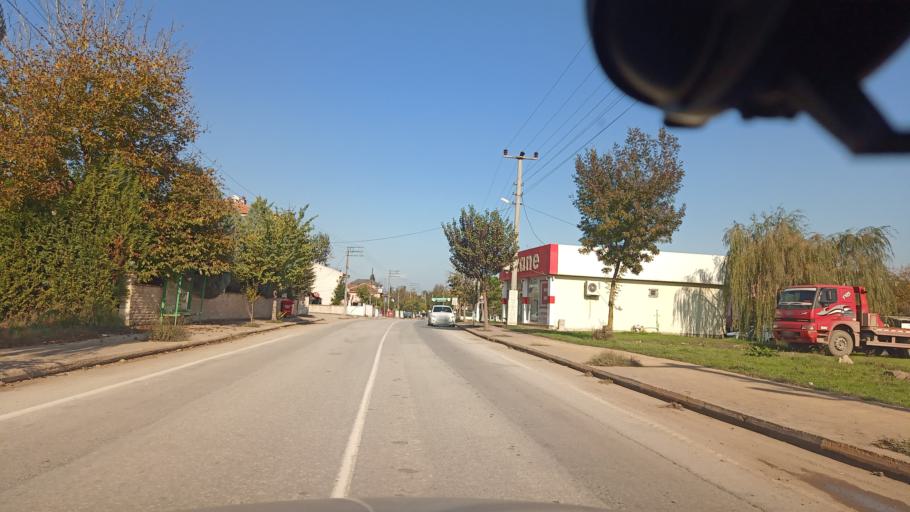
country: TR
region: Sakarya
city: Sogutlu
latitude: 40.8936
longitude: 30.4681
